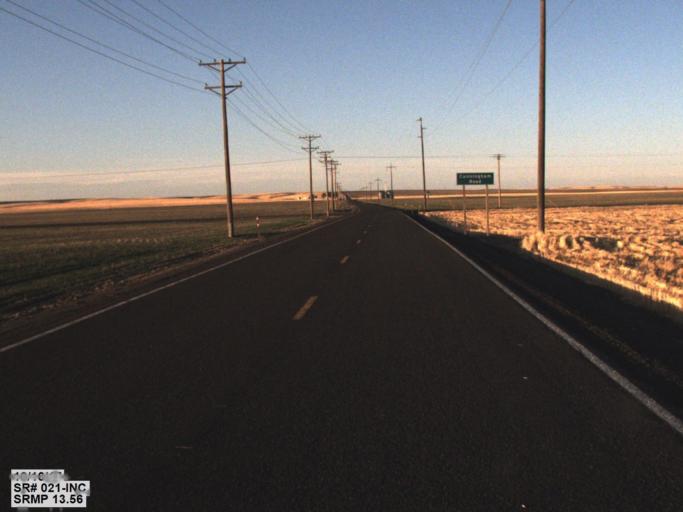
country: US
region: Washington
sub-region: Adams County
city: Ritzville
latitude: 46.8226
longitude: -118.5469
